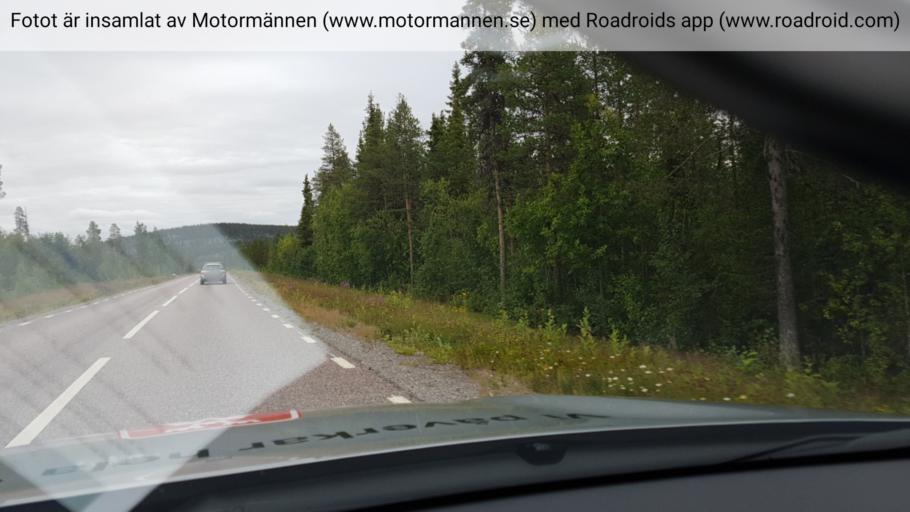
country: SE
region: Norrbotten
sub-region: Gallivare Kommun
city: Gaellivare
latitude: 67.0327
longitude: 21.7086
